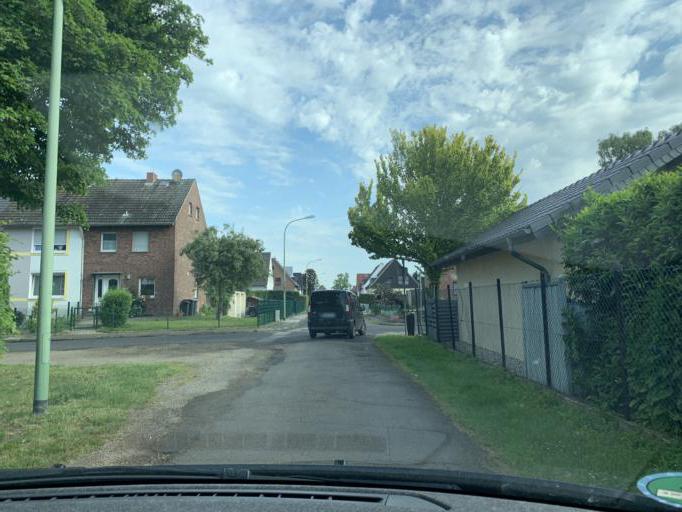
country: DE
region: North Rhine-Westphalia
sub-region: Regierungsbezirk Koln
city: Kreuzau
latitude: 50.7538
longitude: 6.5219
